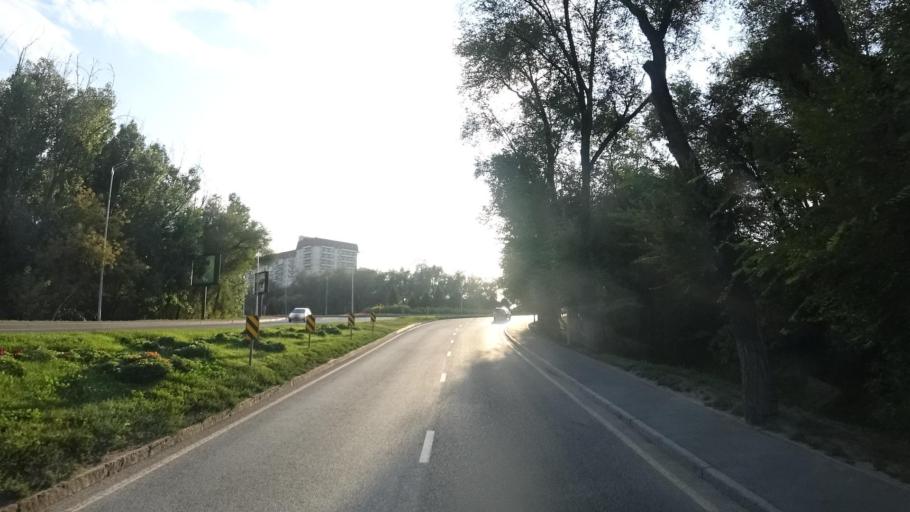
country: KZ
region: Almaty Oblysy
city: Pervomayskiy
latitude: 43.3436
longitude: 76.9970
